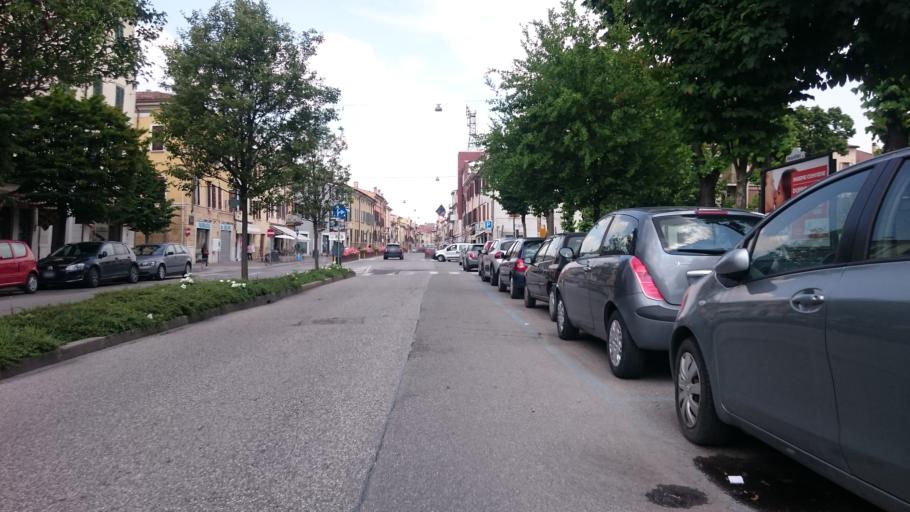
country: IT
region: Lombardy
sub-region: Provincia di Mantova
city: Mantova
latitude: 45.1502
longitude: 10.7960
